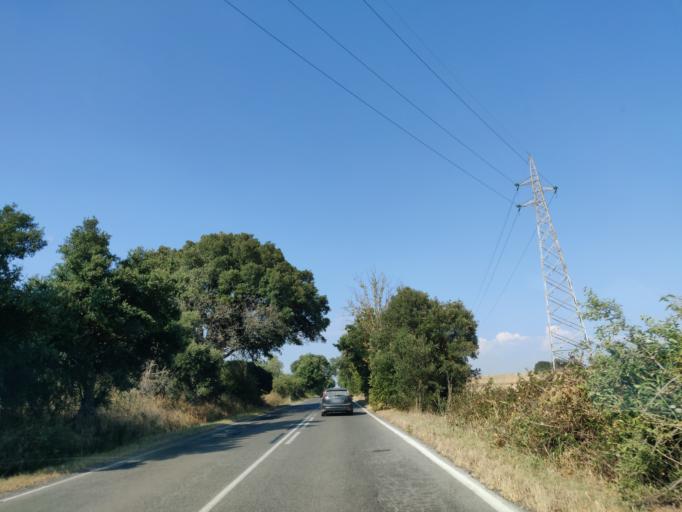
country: IT
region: Latium
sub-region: Provincia di Viterbo
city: Montalto di Castro
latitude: 42.3724
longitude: 11.6505
